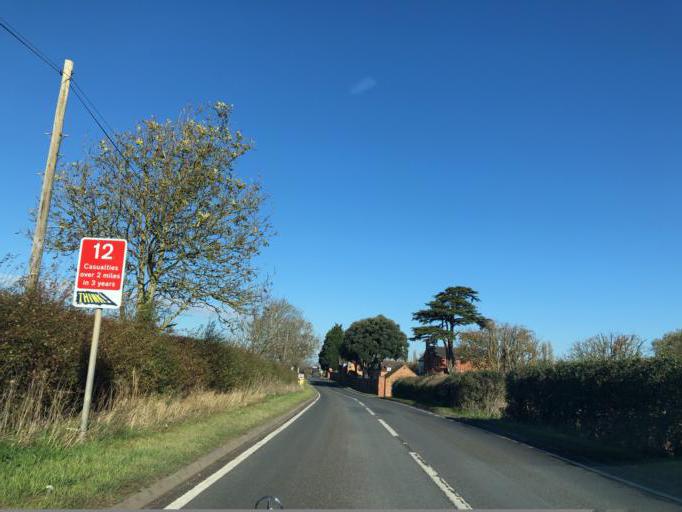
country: GB
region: England
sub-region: Warwickshire
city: Harbury
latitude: 52.2647
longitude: -1.4754
